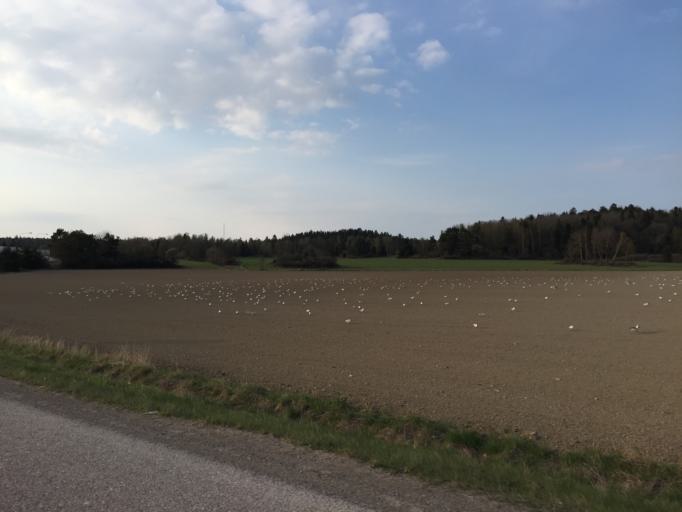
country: SE
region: Stockholm
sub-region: Sodertalje Kommun
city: Pershagen
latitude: 59.0856
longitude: 17.6054
